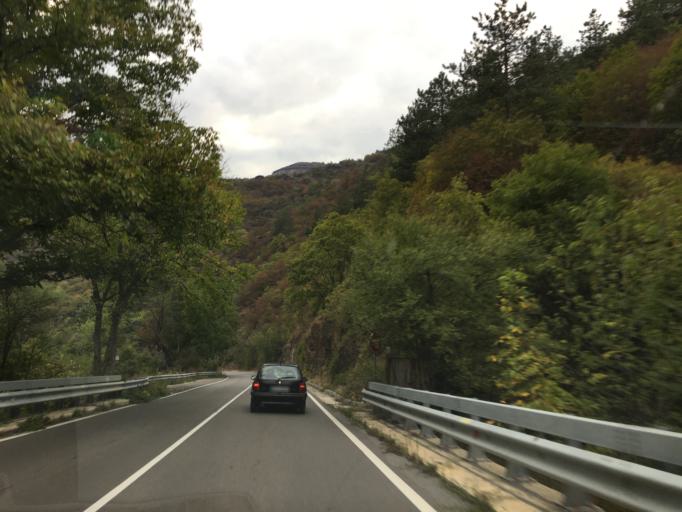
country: BG
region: Sofiya
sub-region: Obshtina Svoge
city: Bov
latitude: 43.0454
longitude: 23.3568
